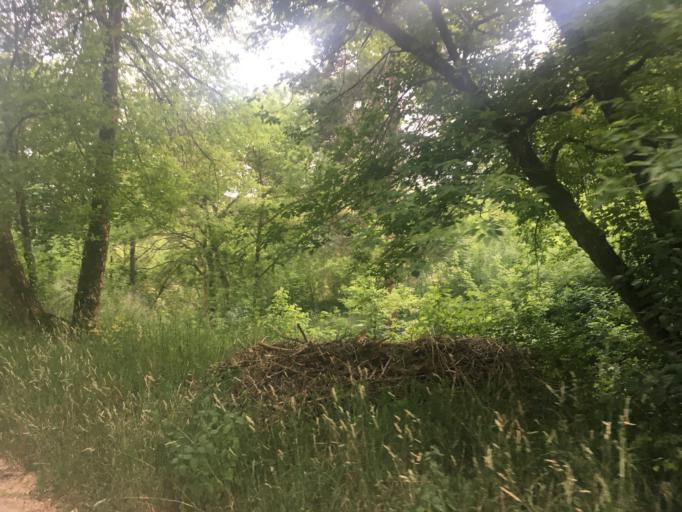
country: BY
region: Grodnenskaya
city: Hrodna
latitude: 53.6806
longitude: 23.8083
